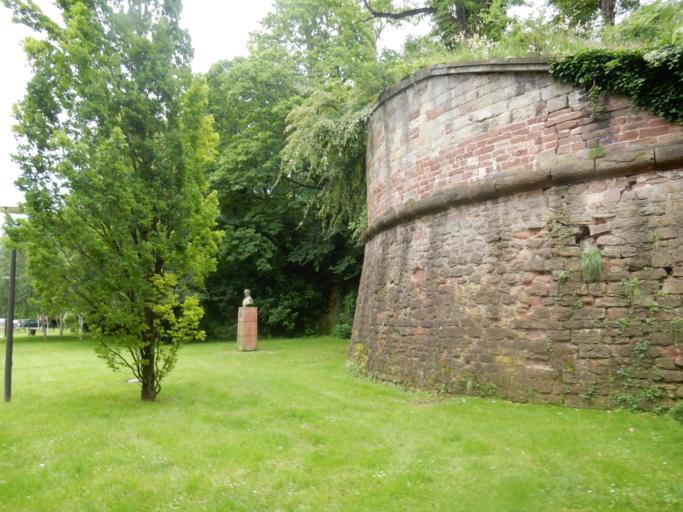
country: FR
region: Alsace
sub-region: Departement du Bas-Rhin
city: Strasbourg
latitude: 48.5757
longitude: 7.7715
